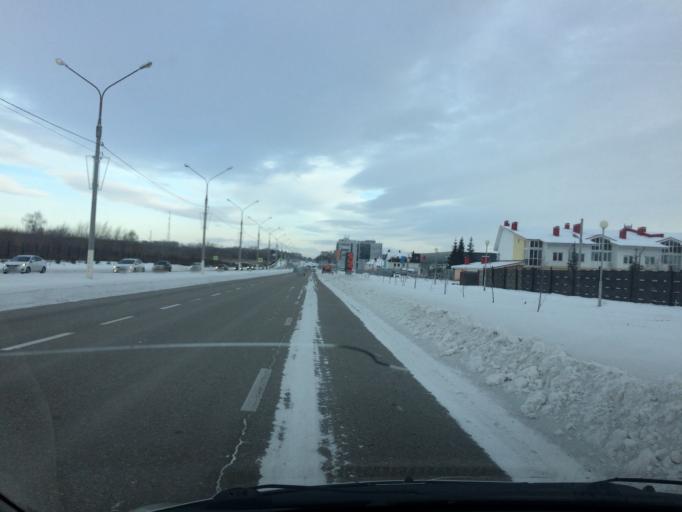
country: RU
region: Chelyabinsk
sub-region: Gorod Magnitogorsk
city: Magnitogorsk
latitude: 53.3821
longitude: 58.9618
